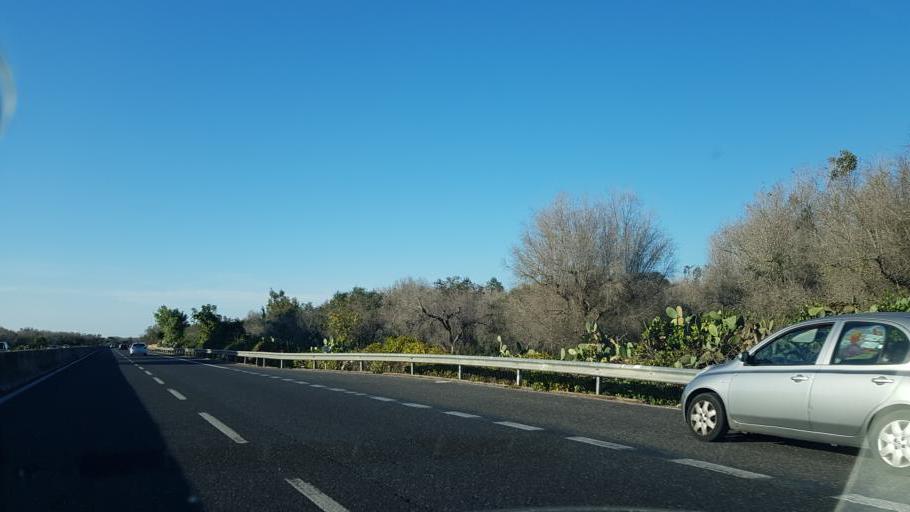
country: IT
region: Apulia
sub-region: Provincia di Brindisi
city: Torchiarolo
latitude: 40.4650
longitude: 18.0559
